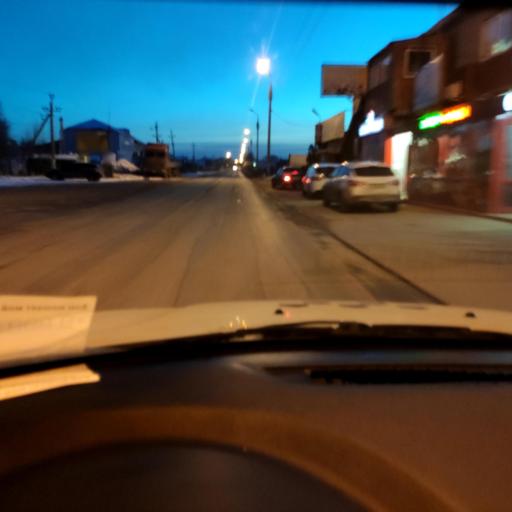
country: RU
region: Samara
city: Tol'yatti
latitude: 53.5666
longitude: 49.3969
